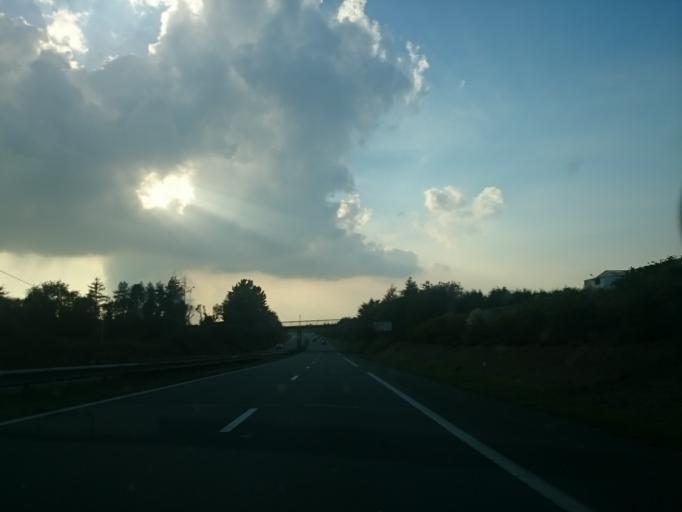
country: FR
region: Brittany
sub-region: Departement du Finistere
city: Landivisiau
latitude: 48.5185
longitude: -4.0698
